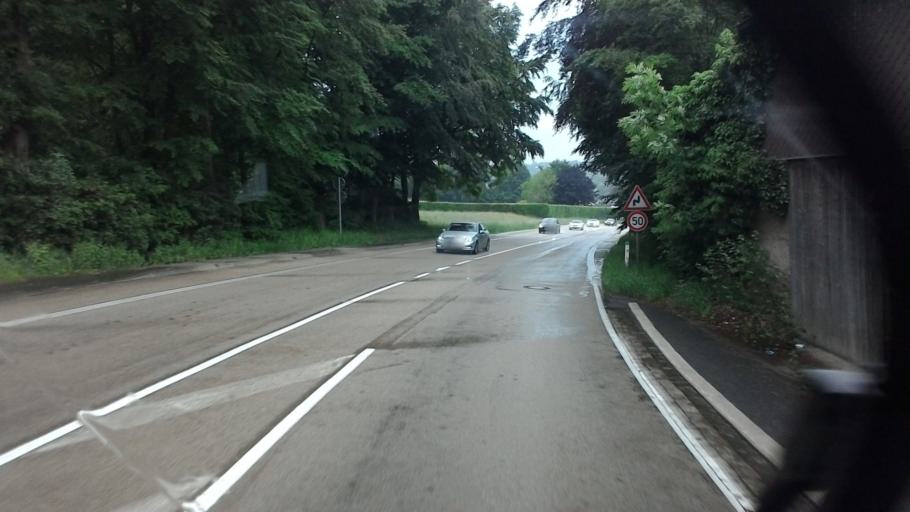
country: DE
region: North Rhine-Westphalia
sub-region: Regierungsbezirk Koln
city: Monschau
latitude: 50.5656
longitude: 6.2515
